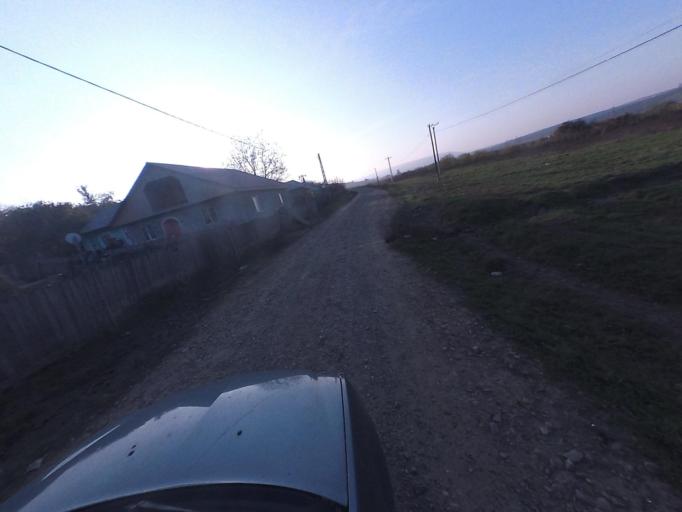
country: RO
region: Vaslui
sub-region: Comuna Bacesti
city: Bacesti
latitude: 46.8113
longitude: 27.2340
